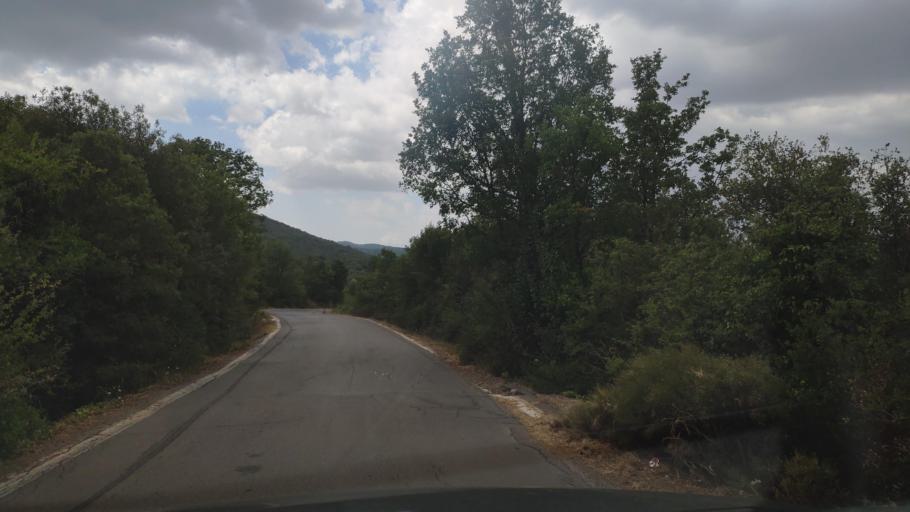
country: GR
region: Peloponnese
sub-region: Nomos Lakonias
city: Kariai
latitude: 37.3212
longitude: 22.4331
